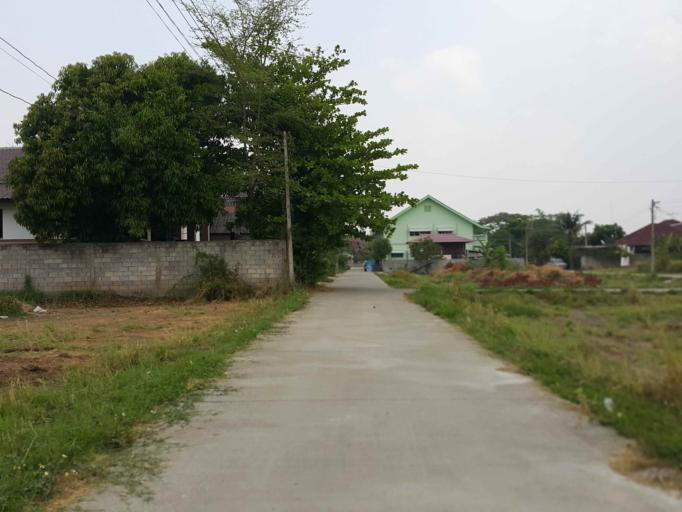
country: TH
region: Chiang Mai
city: Saraphi
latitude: 18.7501
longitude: 99.0170
